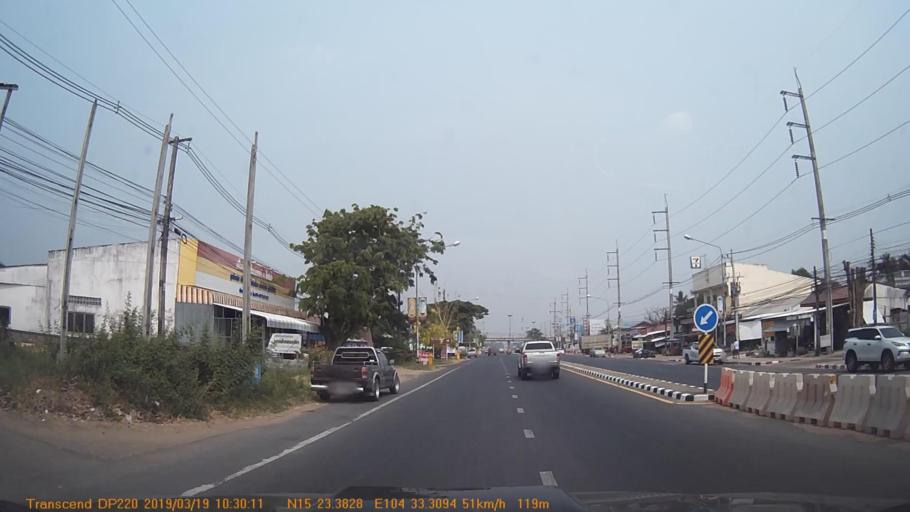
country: TH
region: Changwat Ubon Ratchathani
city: Khueang Nai
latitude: 15.3899
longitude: 104.5551
